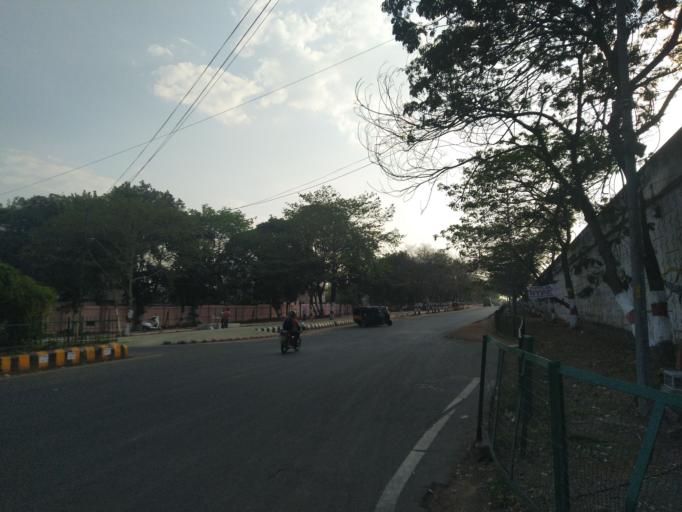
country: IN
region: Odisha
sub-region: Khordha
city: Bhubaneshwar
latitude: 20.2951
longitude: 85.8248
